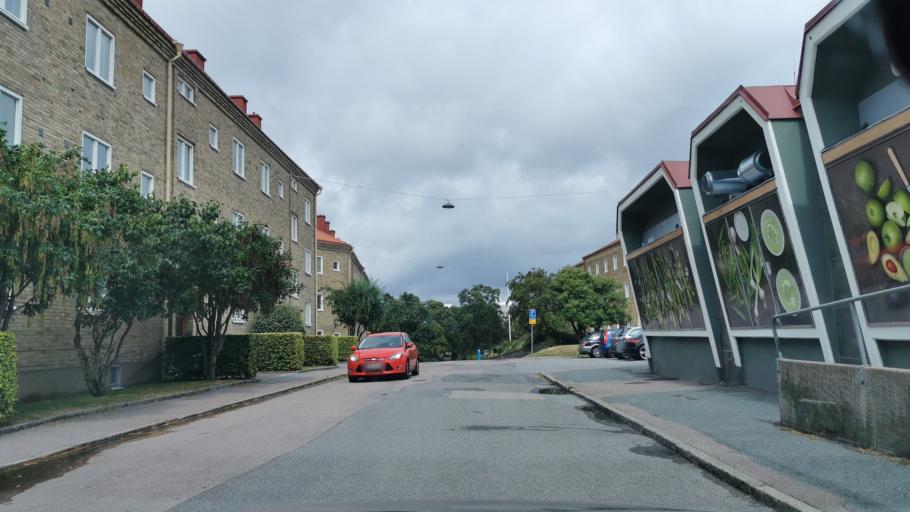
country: SE
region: Vaestra Goetaland
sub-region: Goteborg
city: Goeteborg
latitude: 57.6811
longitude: 11.9747
